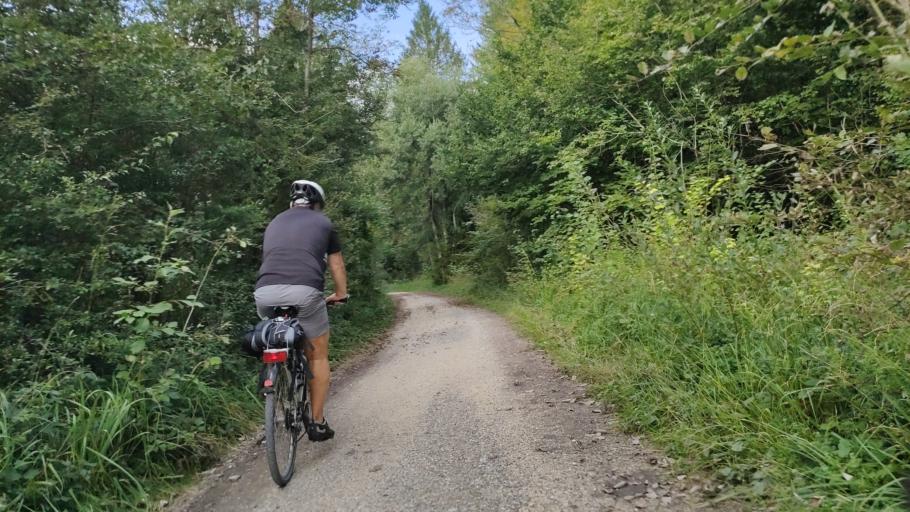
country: DE
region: Bavaria
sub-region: Upper Bavaria
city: Kaufering
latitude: 48.1229
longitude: 10.8584
